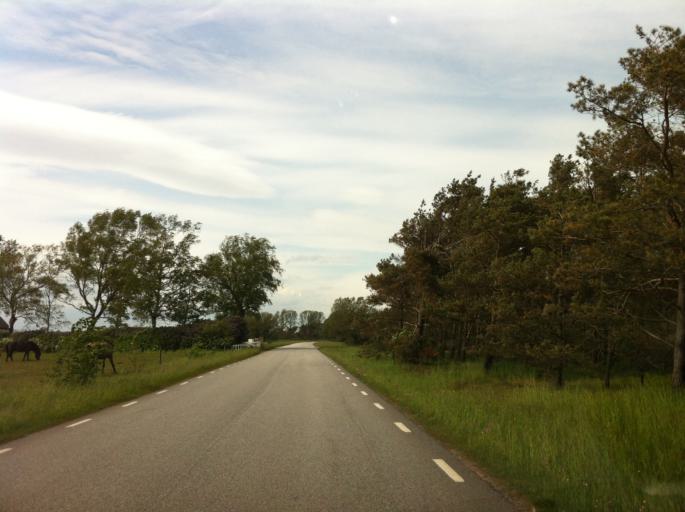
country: SE
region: Skane
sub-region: Kavlinge Kommun
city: Hofterup
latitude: 55.8140
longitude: 12.9359
